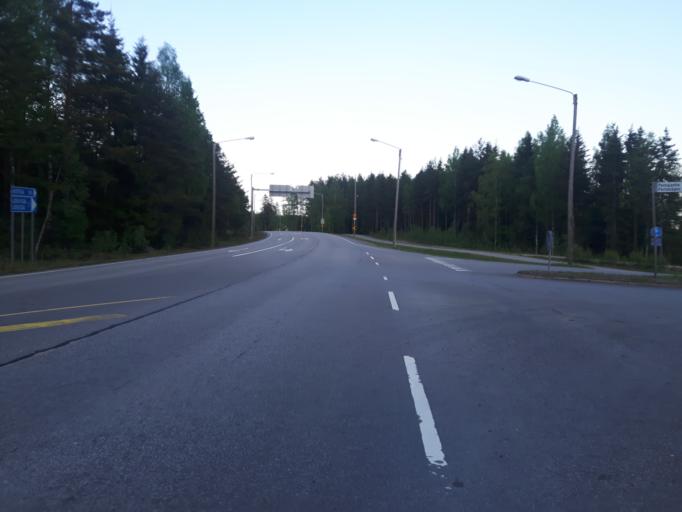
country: FI
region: Uusimaa
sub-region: Loviisa
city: Perna
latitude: 60.4539
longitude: 26.0979
